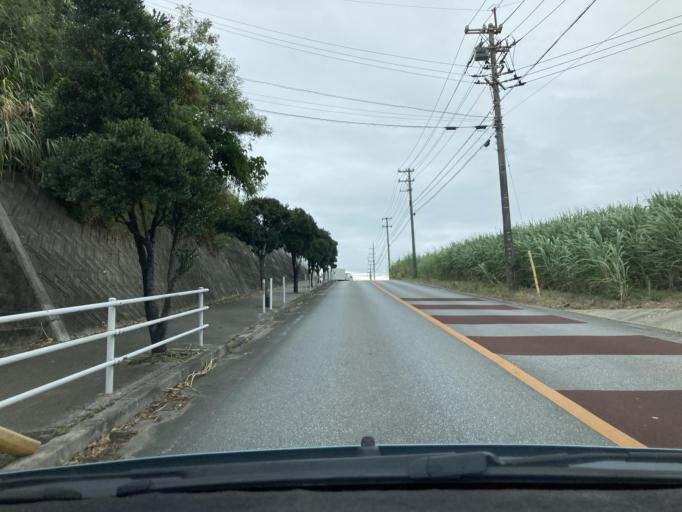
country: JP
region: Okinawa
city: Tomigusuku
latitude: 26.1630
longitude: 127.7082
